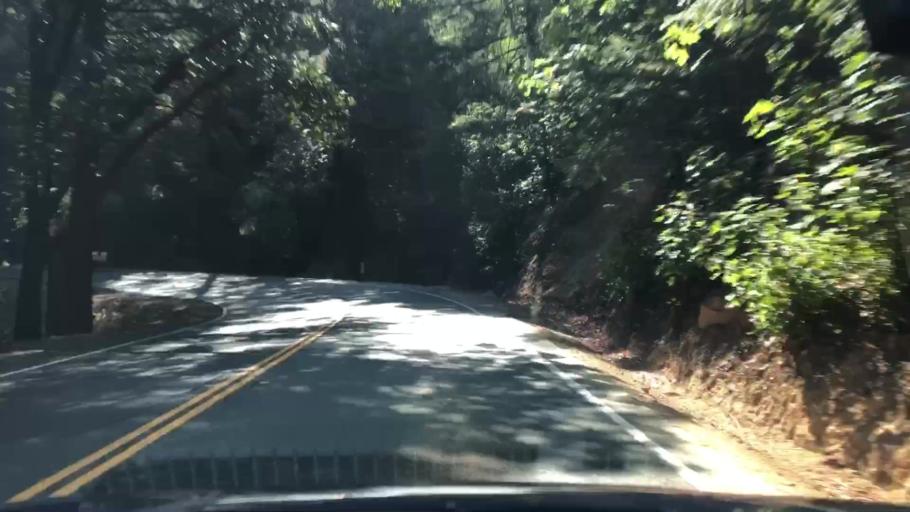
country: US
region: California
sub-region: Napa County
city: Calistoga
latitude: 38.6601
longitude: -122.5983
